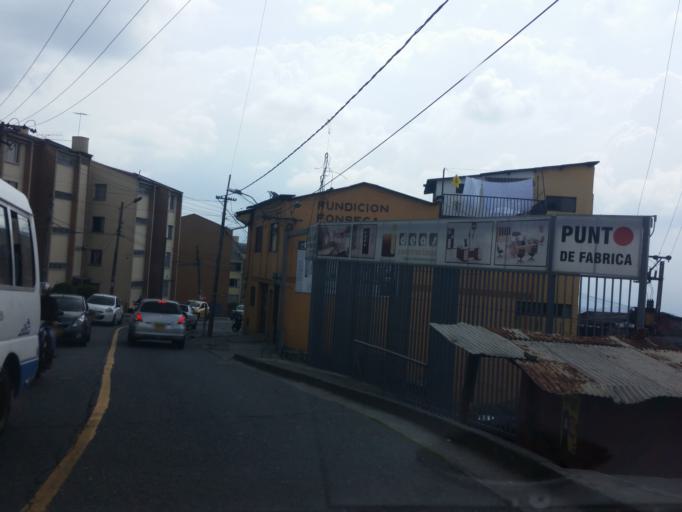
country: CO
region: Caldas
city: Manizales
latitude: 5.0645
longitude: -75.5079
